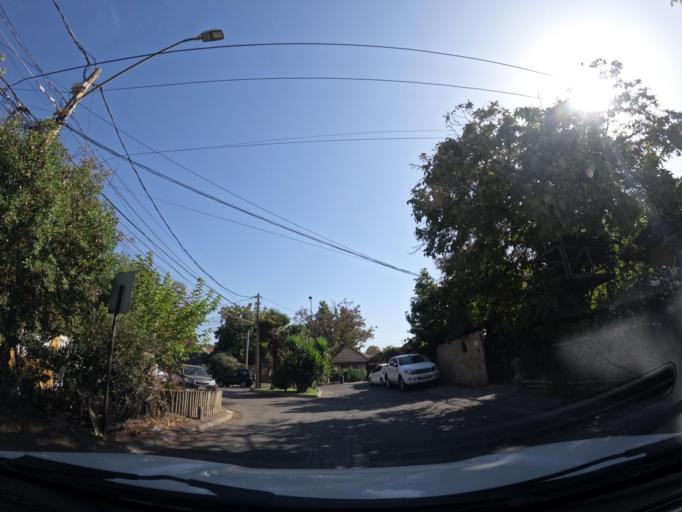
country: CL
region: Santiago Metropolitan
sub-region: Provincia de Santiago
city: Villa Presidente Frei, Nunoa, Santiago, Chile
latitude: -33.5061
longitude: -70.5569
